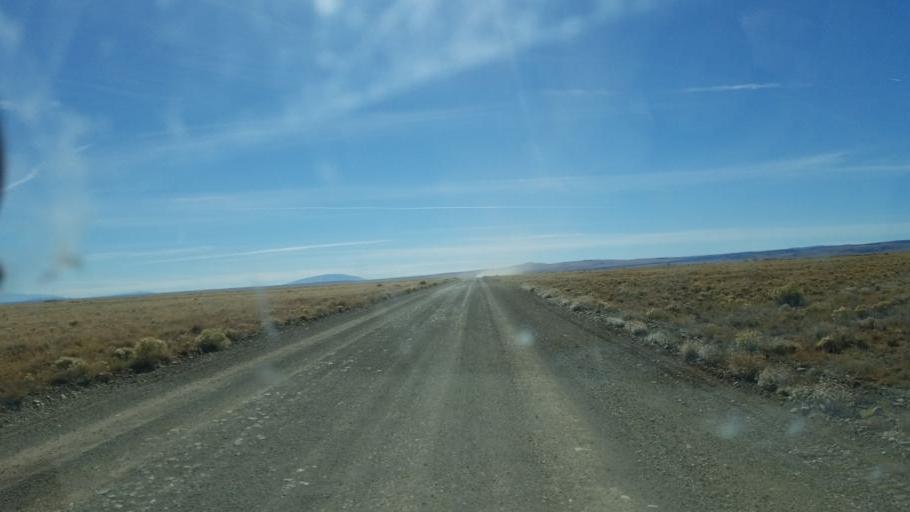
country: US
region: Colorado
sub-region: Rio Grande County
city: Monte Vista
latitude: 37.3386
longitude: -106.1490
